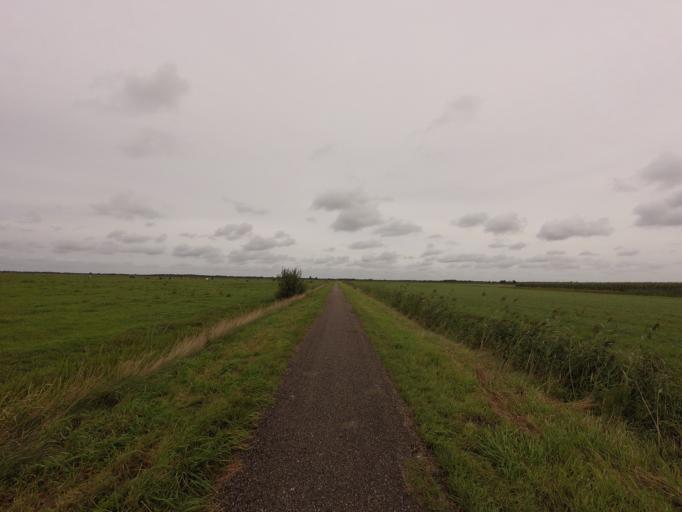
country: NL
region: Overijssel
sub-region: Gemeente Steenwijkerland
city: Blokzijl
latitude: 52.7592
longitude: 5.9246
